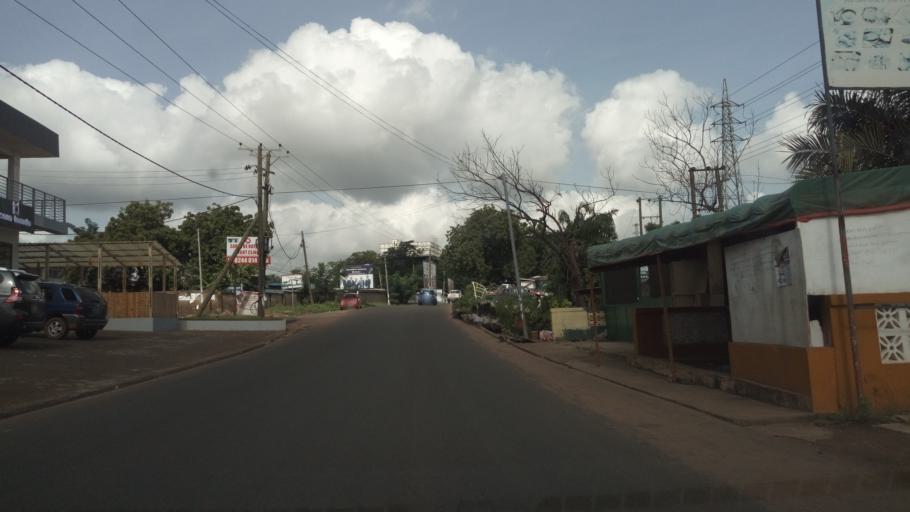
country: GH
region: Greater Accra
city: Medina Estates
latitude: 5.6593
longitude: -0.1592
